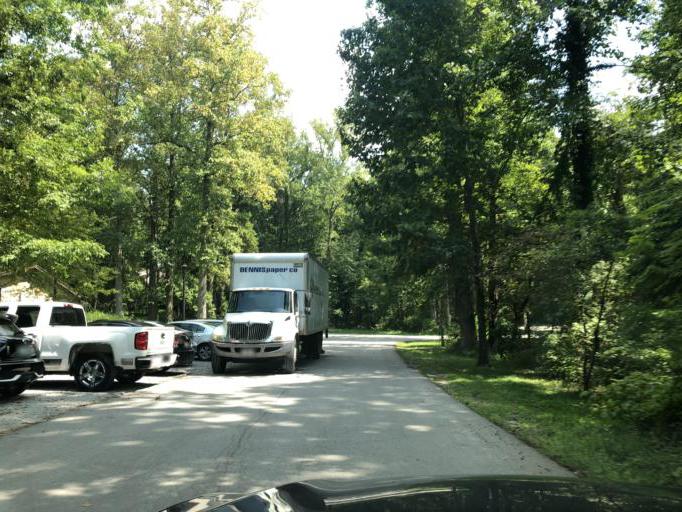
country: US
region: Tennessee
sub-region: Franklin County
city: Sewanee
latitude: 35.2019
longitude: -85.9196
